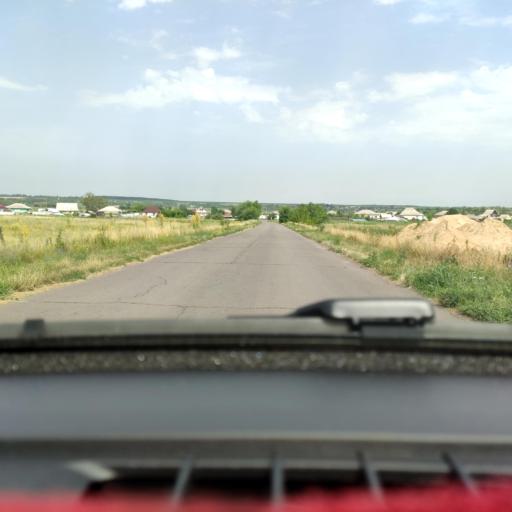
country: RU
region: Voronezj
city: Davydovka
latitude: 51.1933
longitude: 39.4943
